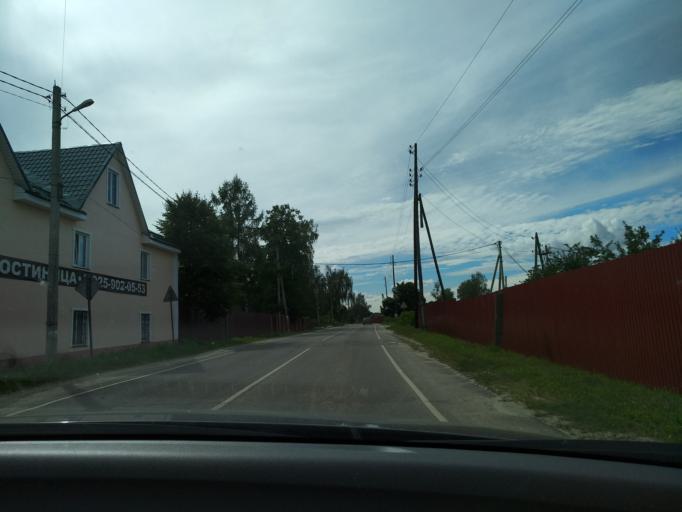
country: RU
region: Moskovskaya
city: Krasnyy Tkach
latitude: 55.3929
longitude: 39.1551
